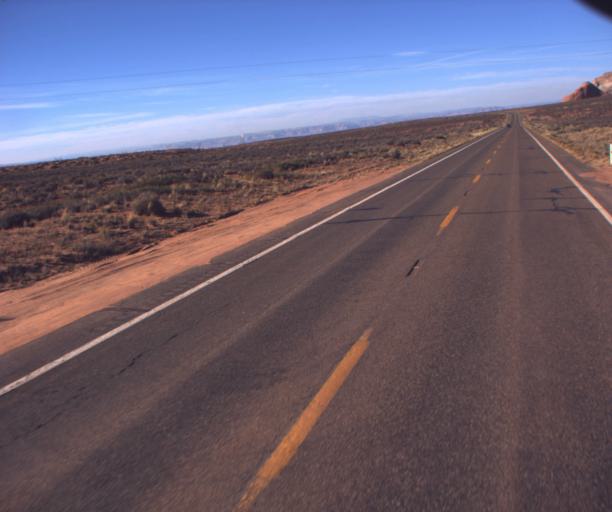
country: US
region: Arizona
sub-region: Coconino County
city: LeChee
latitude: 36.8202
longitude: -111.3077
